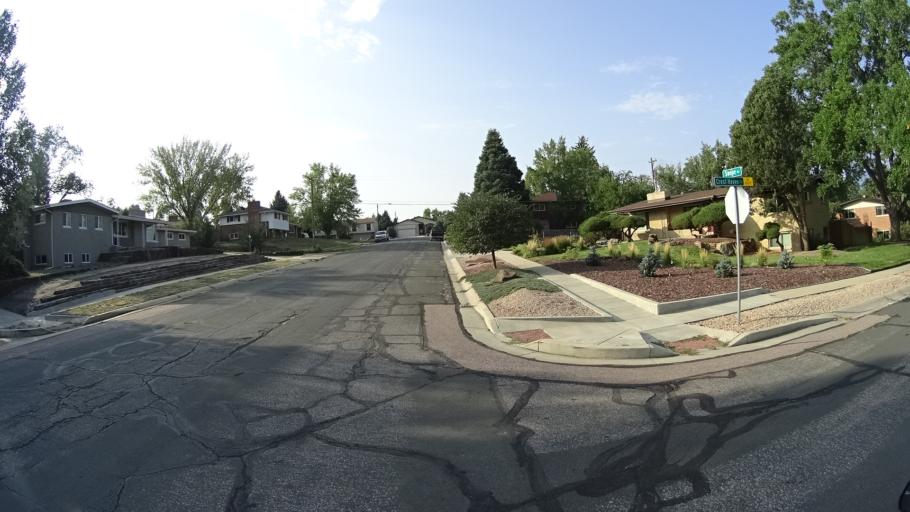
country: US
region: Colorado
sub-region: El Paso County
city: Colorado Springs
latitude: 38.8512
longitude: -104.7915
